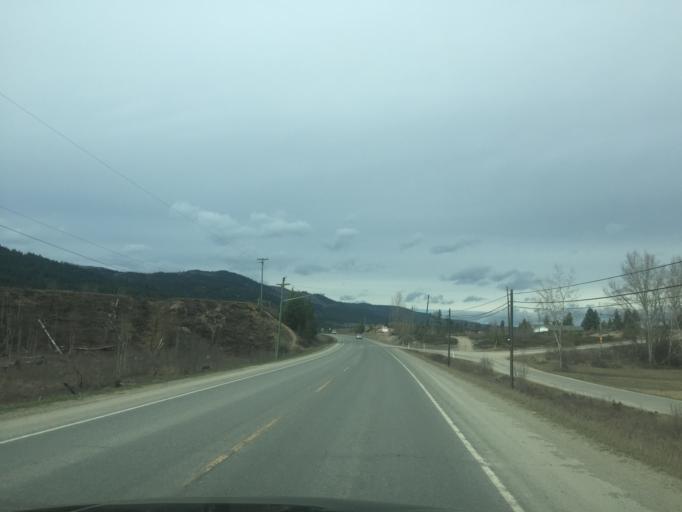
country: CA
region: British Columbia
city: Kamloops
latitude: 51.1815
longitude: -120.1371
